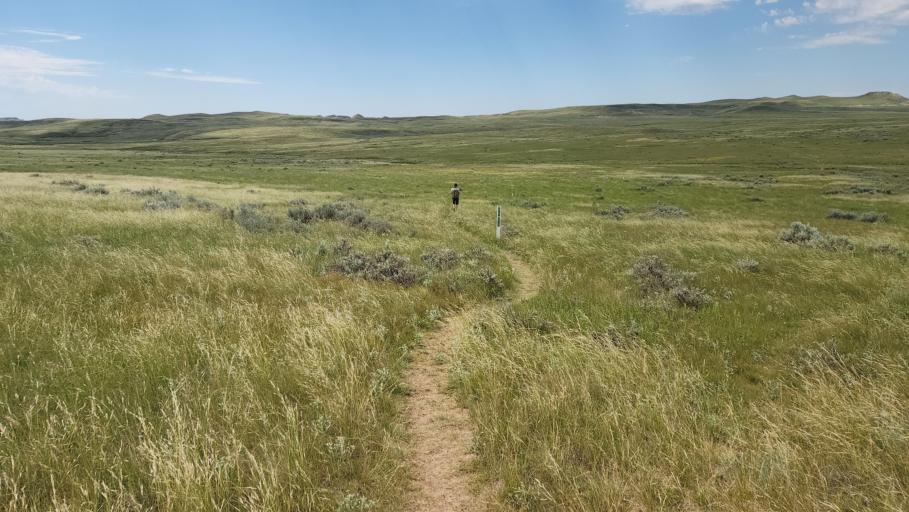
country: CA
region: Saskatchewan
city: Assiniboia
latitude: 49.0760
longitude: -106.5412
